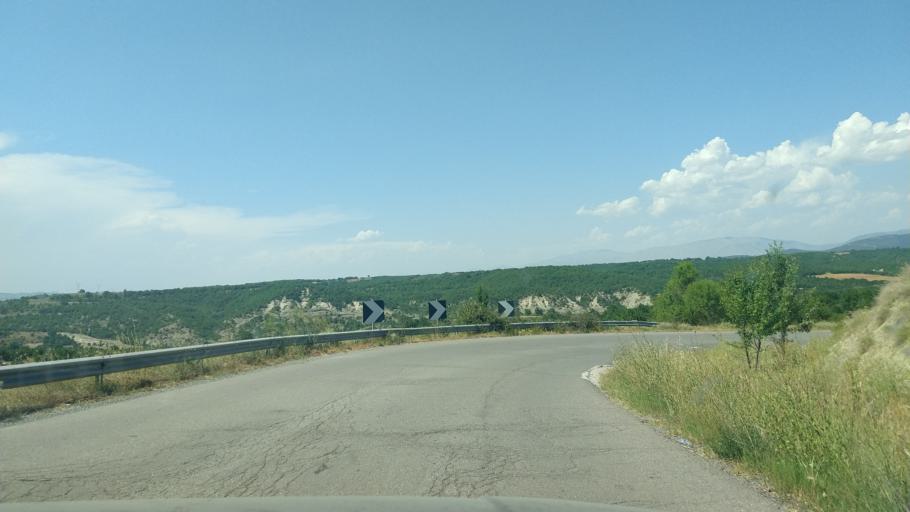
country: GR
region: West Macedonia
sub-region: Nomos Grevenon
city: Grevena
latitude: 40.0413
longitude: 21.4810
